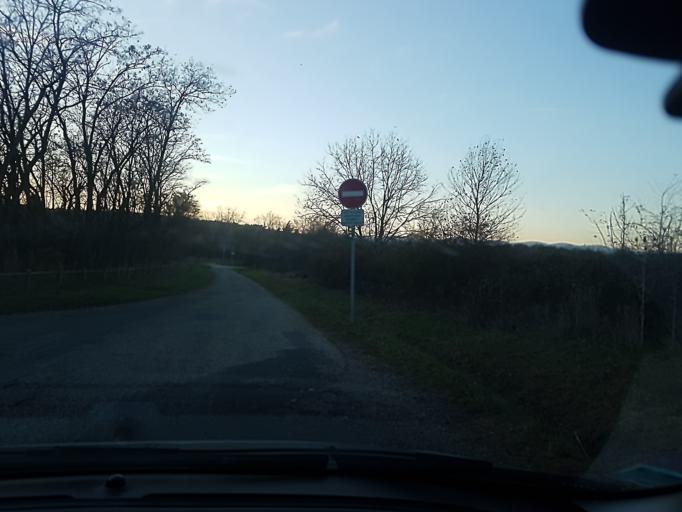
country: FR
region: Rhone-Alpes
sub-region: Departement du Rhone
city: Vourles
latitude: 45.6415
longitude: 4.7677
